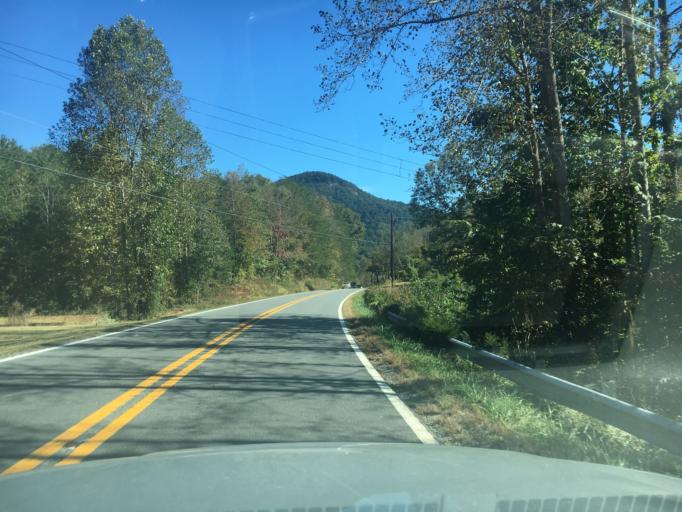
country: US
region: North Carolina
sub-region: Rutherford County
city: Spindale
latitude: 35.5012
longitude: -81.8631
